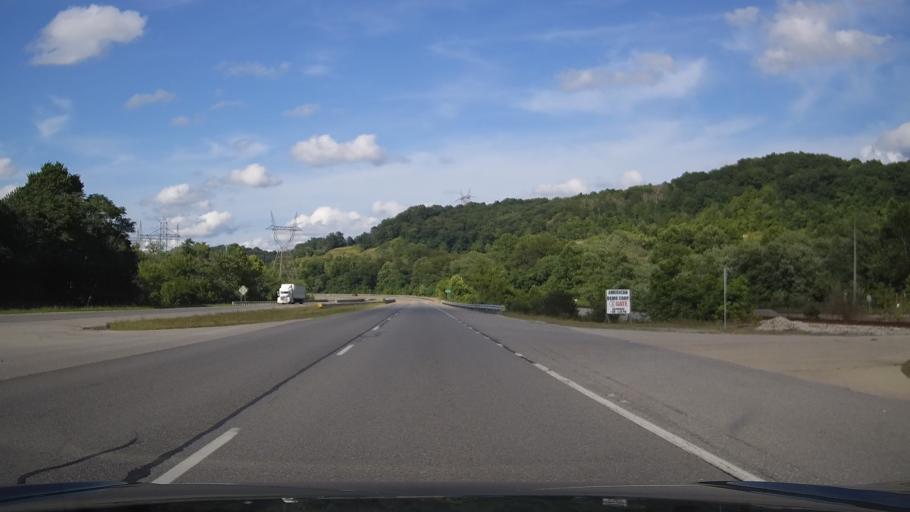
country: US
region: Kentucky
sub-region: Lawrence County
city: Louisa
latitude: 38.1767
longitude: -82.6134
